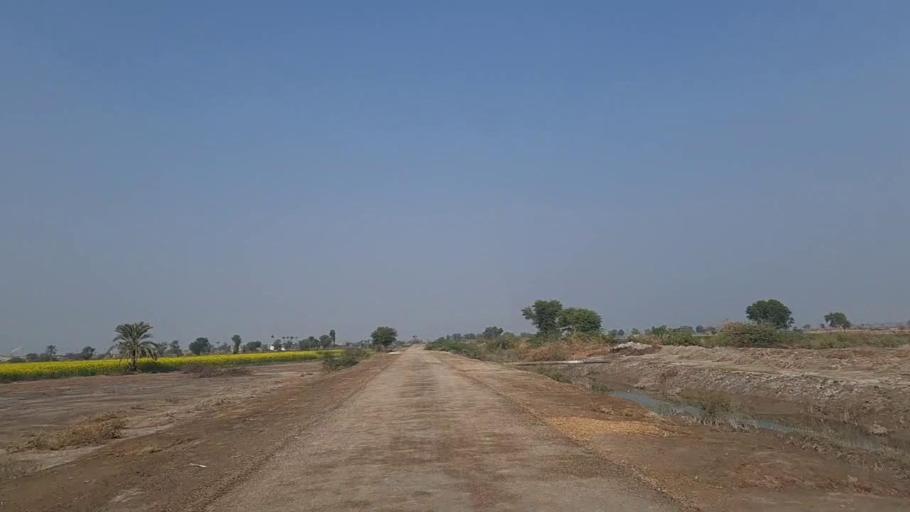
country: PK
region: Sindh
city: Nawabshah
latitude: 26.3647
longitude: 68.4277
